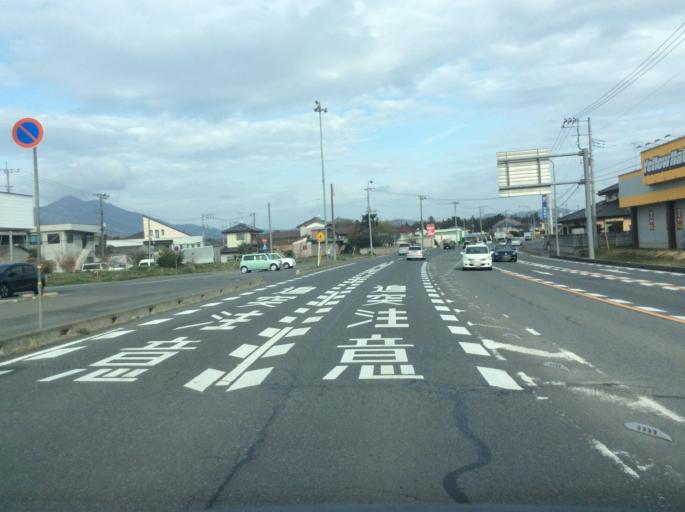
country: JP
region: Ibaraki
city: Tsukuba
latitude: 36.1905
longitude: 140.0156
